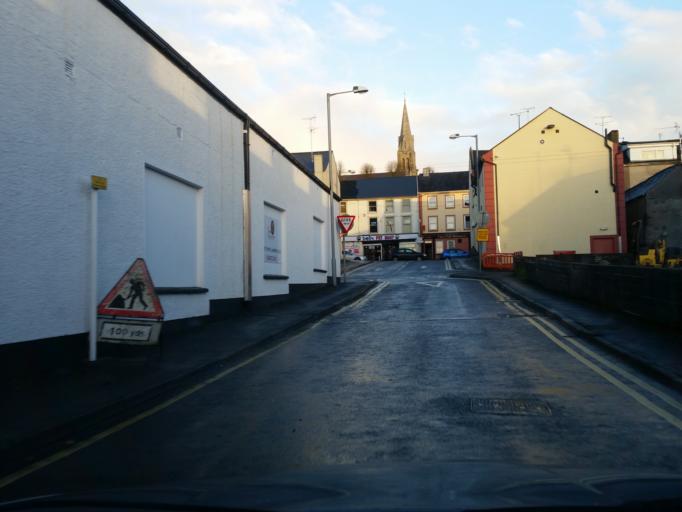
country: GB
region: Northern Ireland
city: Lisnaskea
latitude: 54.2520
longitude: -7.4435
